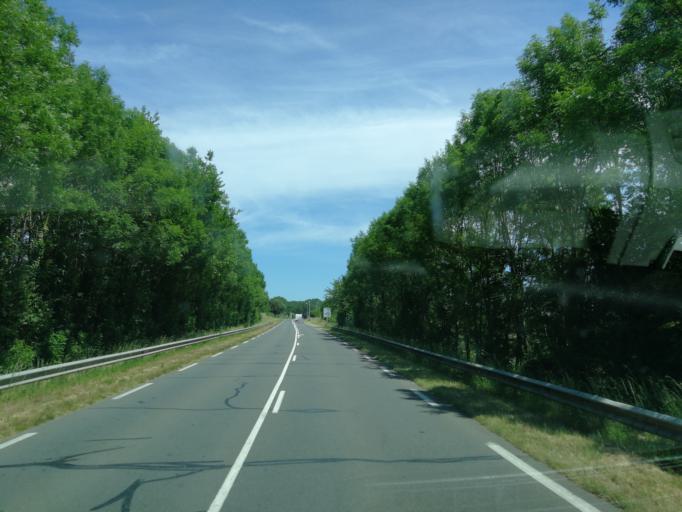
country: FR
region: Pays de la Loire
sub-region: Departement de la Vendee
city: La Chataigneraie
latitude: 46.6387
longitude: -0.7428
